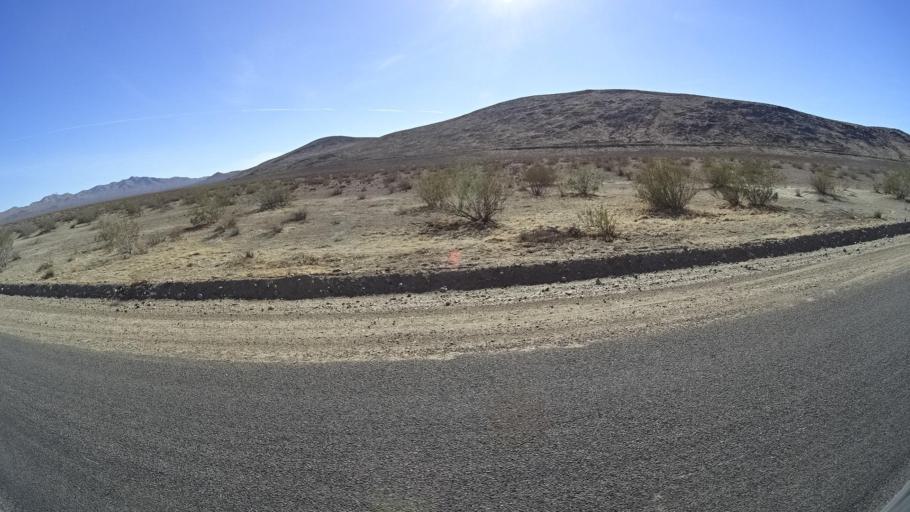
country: US
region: California
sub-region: Kern County
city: China Lake Acres
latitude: 35.5604
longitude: -117.7660
